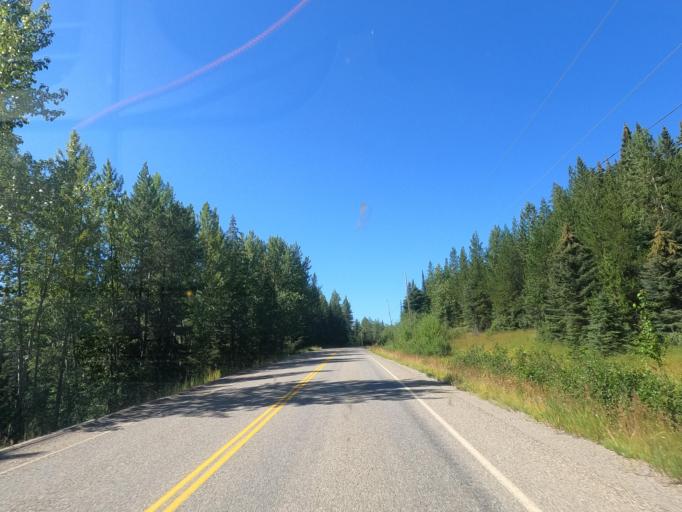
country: CA
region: British Columbia
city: Quesnel
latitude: 53.0355
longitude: -121.9975
